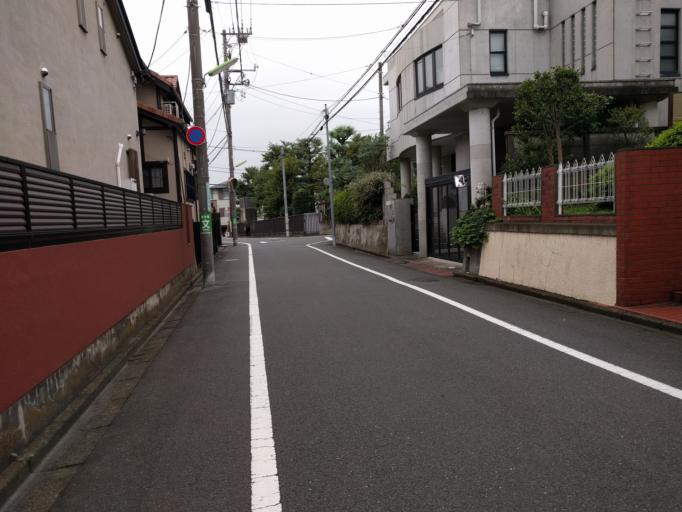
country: JP
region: Tokyo
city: Tokyo
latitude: 35.6165
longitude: 139.6490
